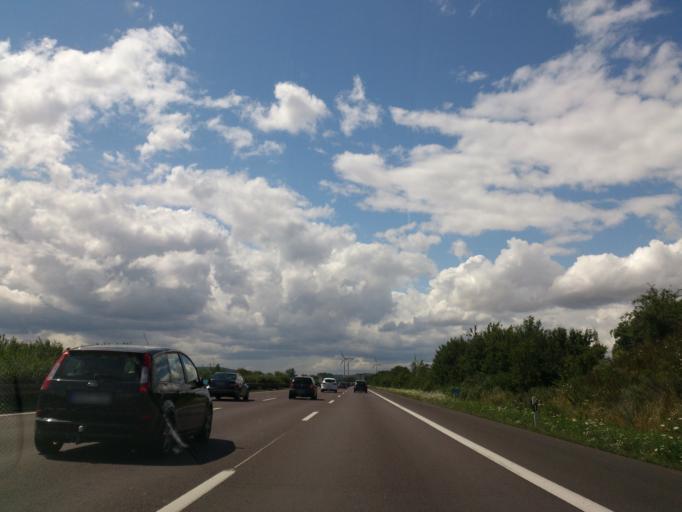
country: DE
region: Lower Saxony
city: Gross Munzel
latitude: 52.3765
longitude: 9.4578
